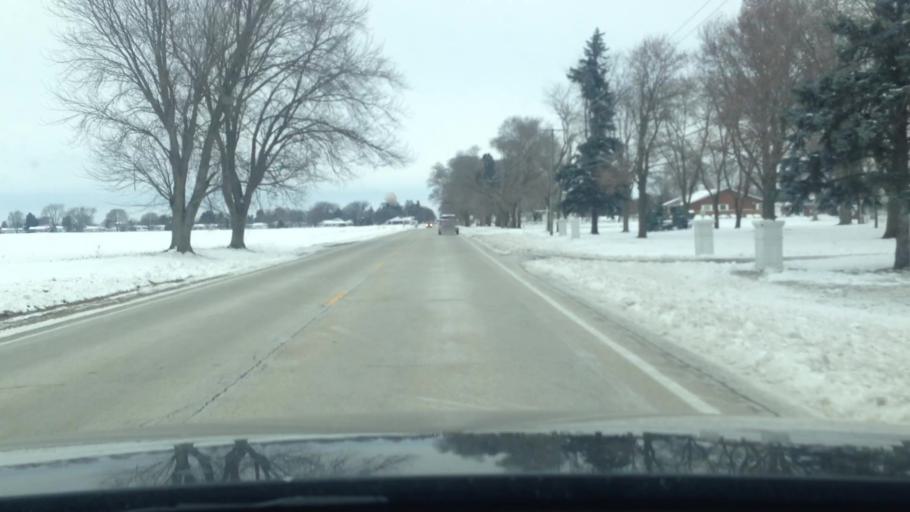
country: US
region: Illinois
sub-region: McHenry County
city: Hebron
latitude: 42.4587
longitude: -88.4329
